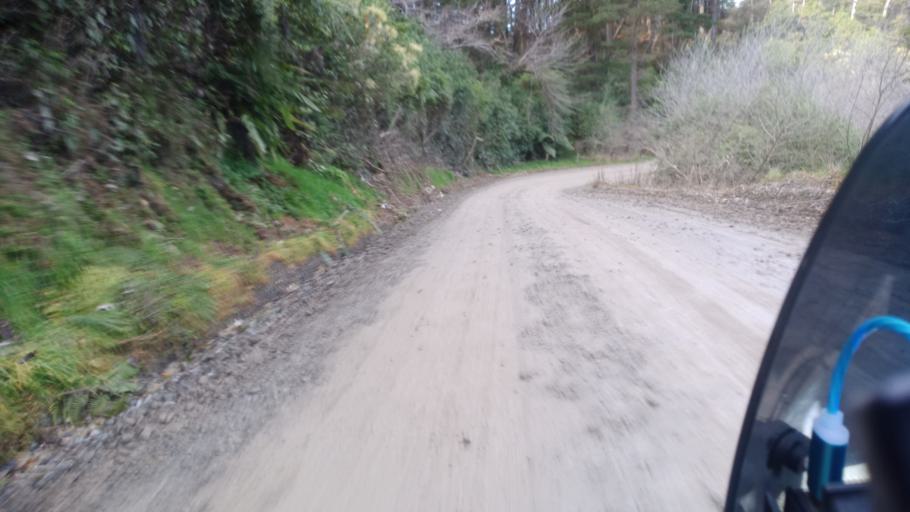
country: NZ
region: Gisborne
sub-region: Gisborne District
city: Gisborne
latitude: -38.1293
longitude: 178.1828
